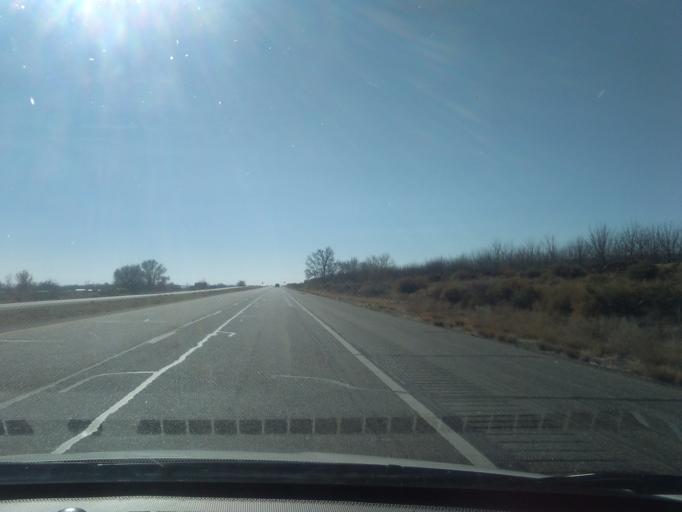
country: US
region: New Mexico
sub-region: Valencia County
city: Jarales
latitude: 34.5841
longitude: -106.7909
